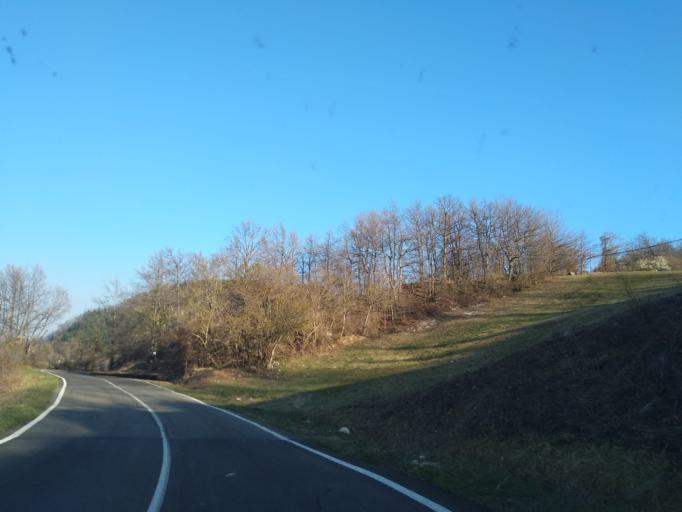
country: IT
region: Emilia-Romagna
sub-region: Provincia di Reggio Emilia
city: Ramiseto
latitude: 44.4150
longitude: 10.2880
